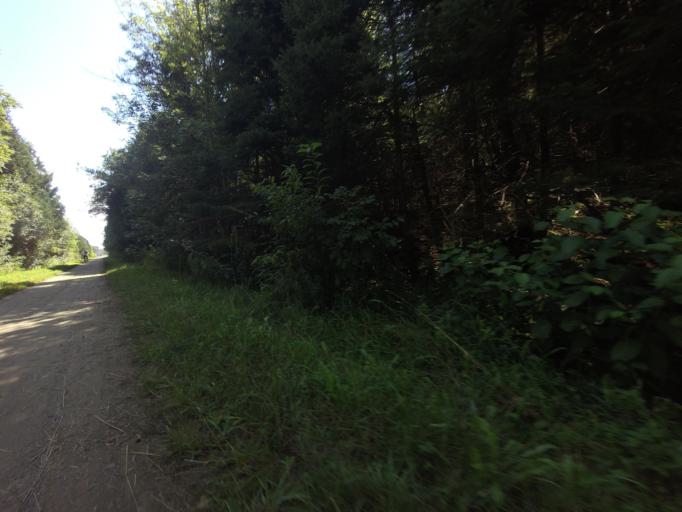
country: CA
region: Ontario
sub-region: Wellington County
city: Guelph
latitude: 43.7360
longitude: -80.3430
